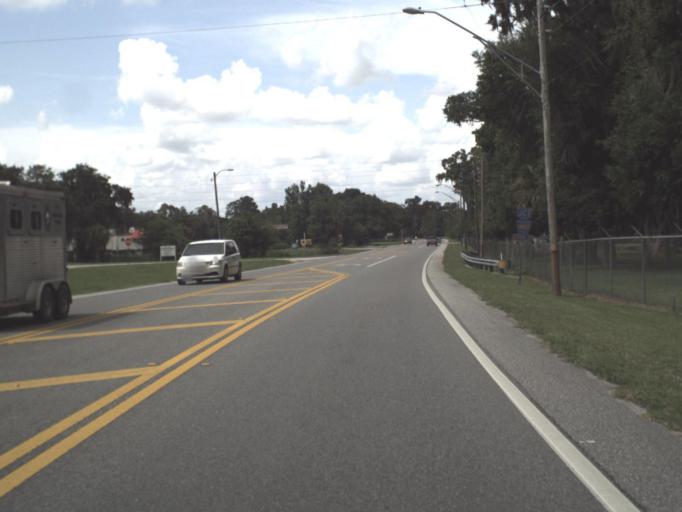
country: US
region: Florida
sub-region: Hernando County
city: Brooksville
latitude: 28.5679
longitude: -82.3755
